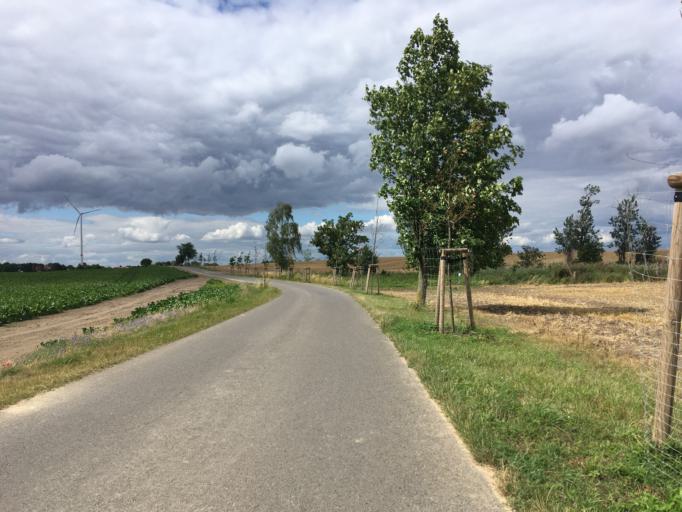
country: DE
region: Brandenburg
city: Gramzow
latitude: 53.2651
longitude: 14.0165
